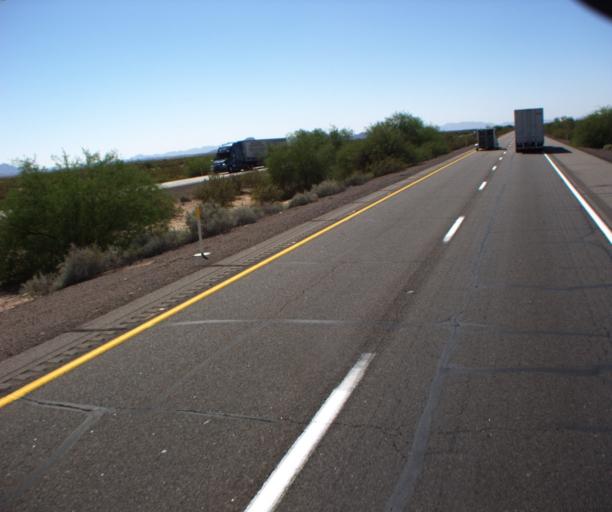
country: US
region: Arizona
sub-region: Yuma County
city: Wellton
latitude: 32.7073
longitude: -113.8640
